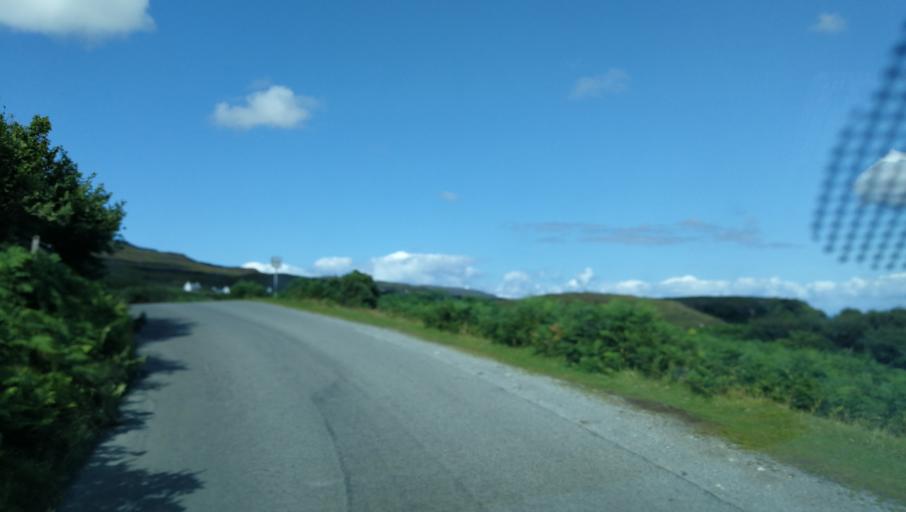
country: GB
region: Scotland
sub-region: Highland
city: Isle of Skye
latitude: 57.4378
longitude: -6.6299
